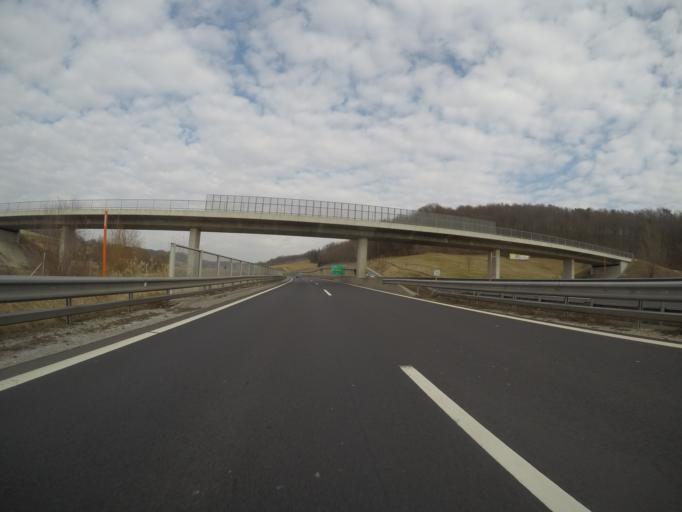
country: SI
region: Cerkvenjak
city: Cerkvenjak
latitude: 46.5564
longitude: 15.9145
